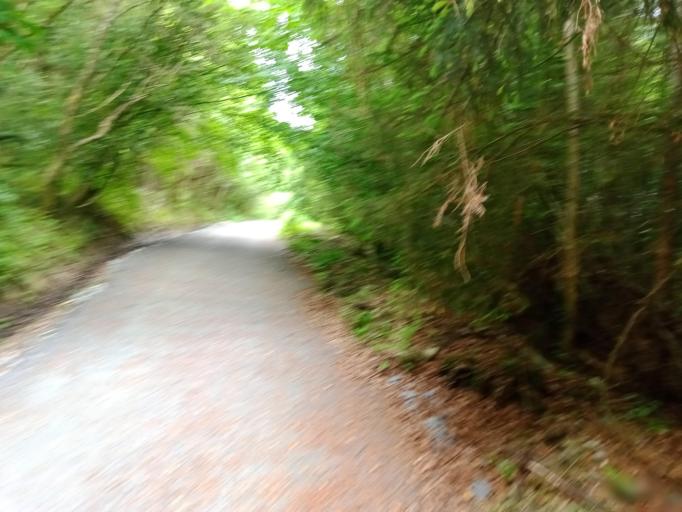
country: IE
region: Leinster
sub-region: Kilkenny
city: Thomastown
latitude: 52.4719
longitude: -7.0459
